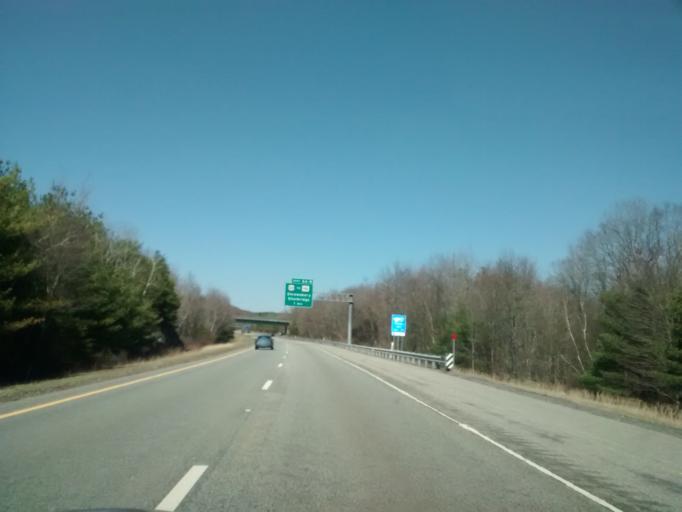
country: US
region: Massachusetts
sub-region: Worcester County
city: Auburn
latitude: 42.1659
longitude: -71.8446
